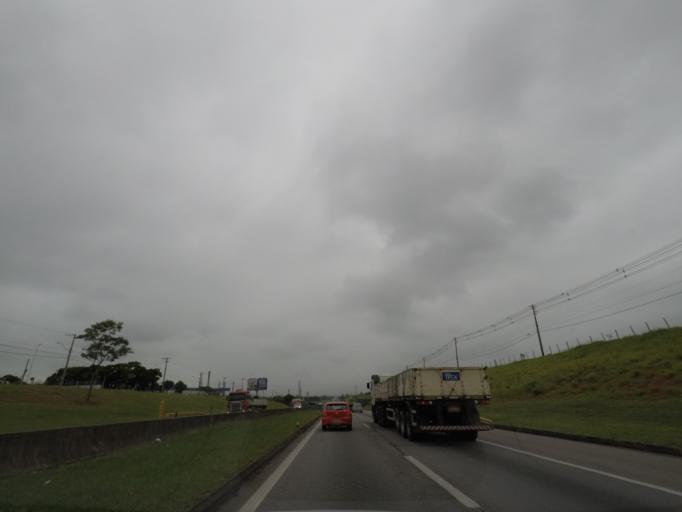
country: BR
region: Sao Paulo
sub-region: Cacapava
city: Cacapava
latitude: -23.1413
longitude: -45.7641
